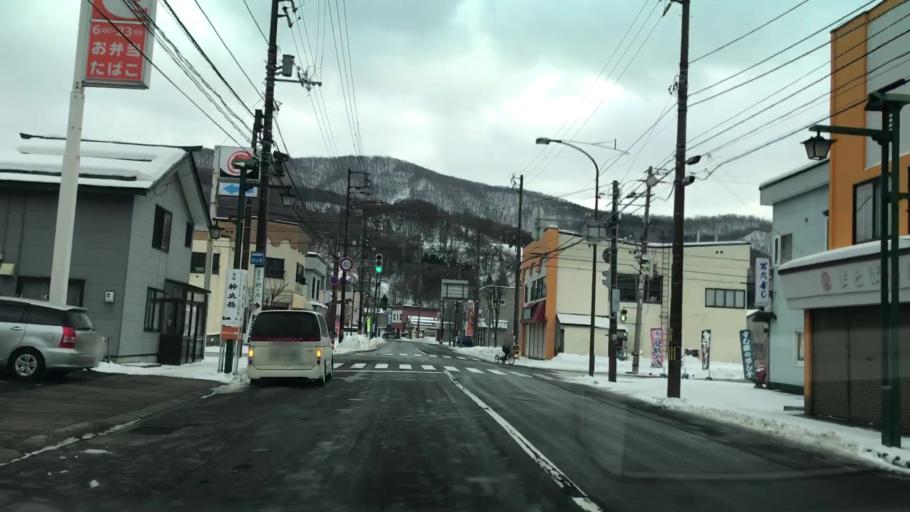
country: JP
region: Hokkaido
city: Yoichi
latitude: 43.2970
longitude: 140.5995
